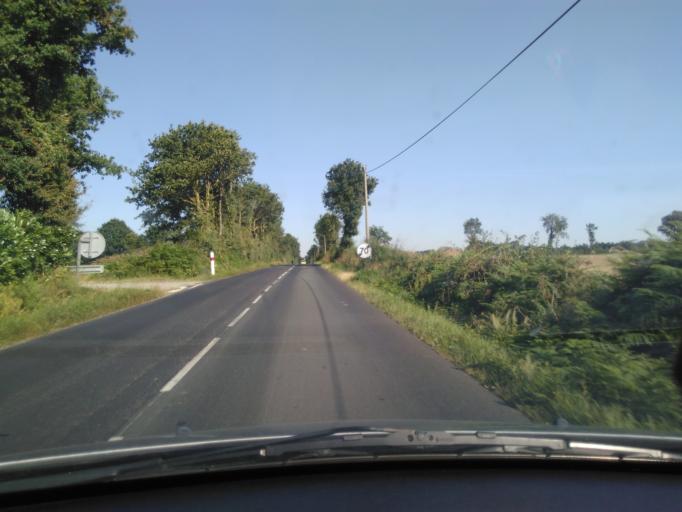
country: FR
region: Pays de la Loire
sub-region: Departement de la Vendee
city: Dompierre-sur-Yon
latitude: 46.7309
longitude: -1.3660
